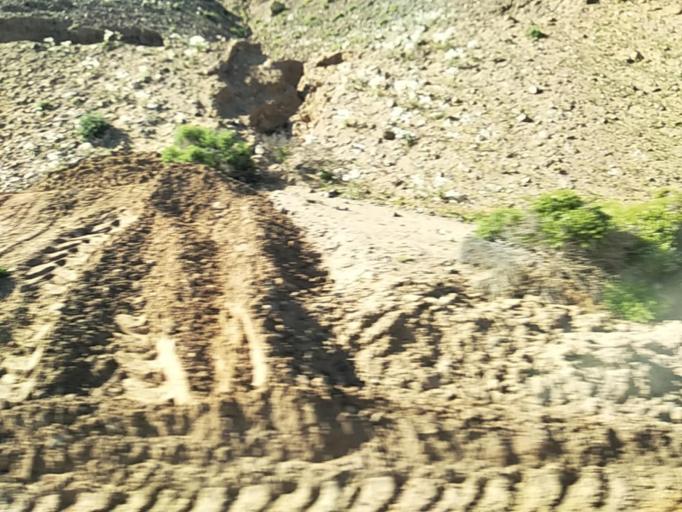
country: CL
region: Atacama
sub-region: Provincia de Copiapo
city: Copiapo
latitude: -27.3358
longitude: -70.7729
